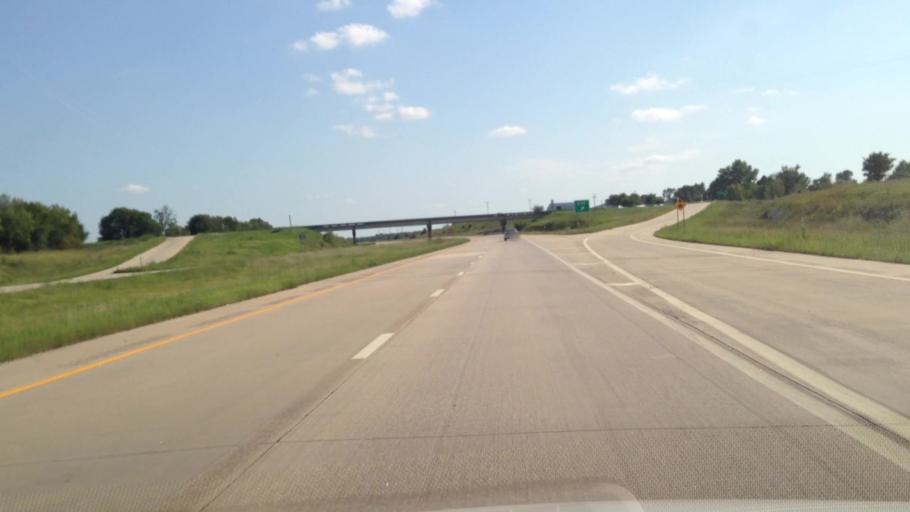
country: US
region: Kansas
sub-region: Bourbon County
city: Fort Scott
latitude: 37.8954
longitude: -94.7052
